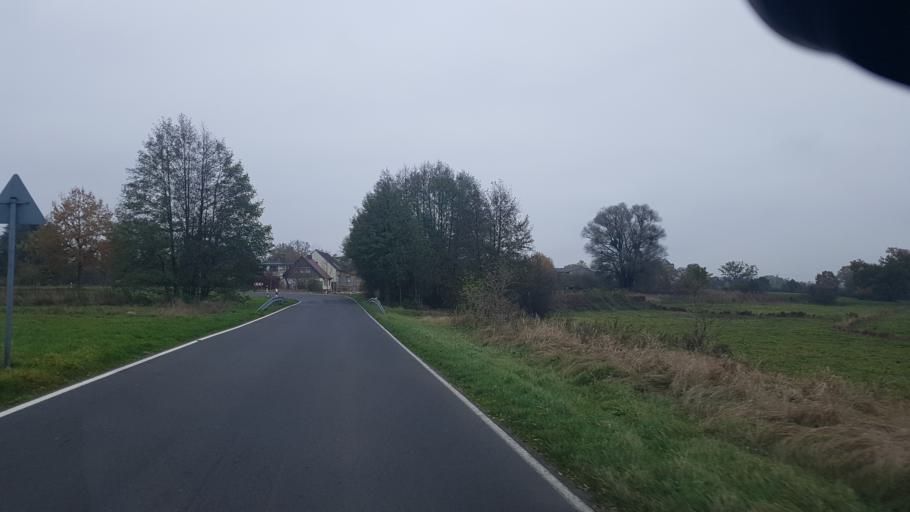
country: DE
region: Brandenburg
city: Schonermark
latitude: 52.9323
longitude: 13.0735
